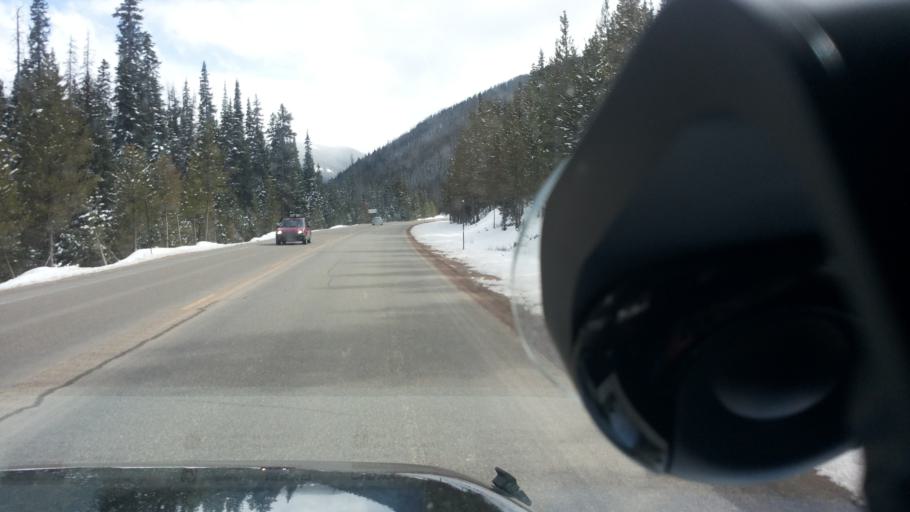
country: US
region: Colorado
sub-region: Grand County
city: Fraser
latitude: 39.8621
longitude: -105.7505
